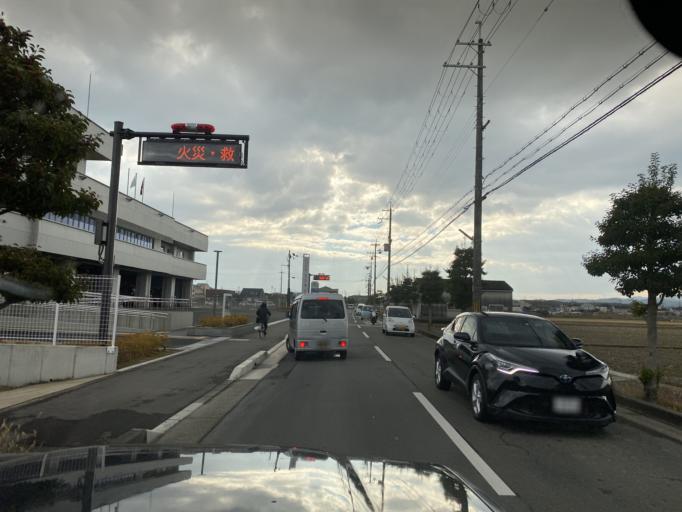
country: JP
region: Kyoto
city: Tanabe
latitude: 34.8449
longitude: 135.7804
